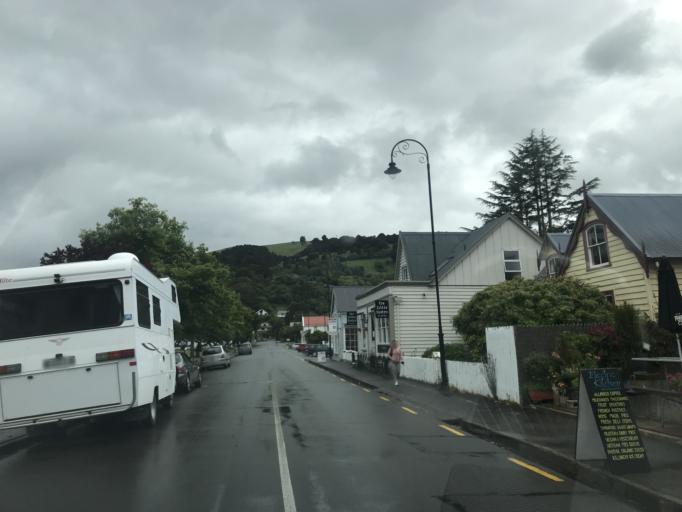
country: NZ
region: Canterbury
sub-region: Christchurch City
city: Christchurch
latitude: -43.8030
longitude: 172.9687
